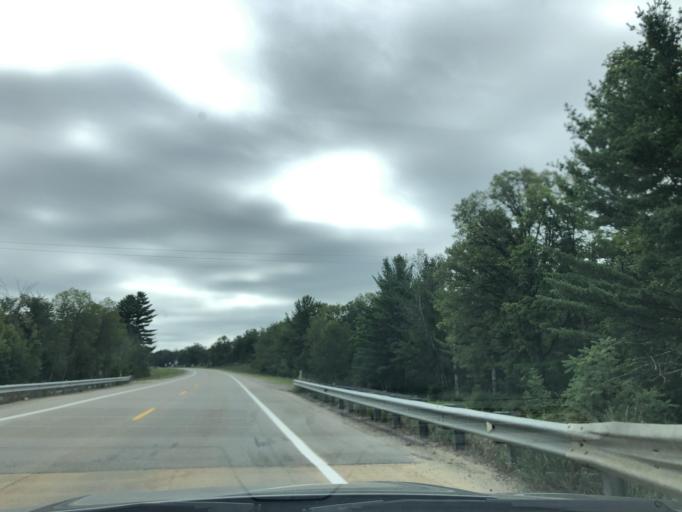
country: US
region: Michigan
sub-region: Clare County
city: Harrison
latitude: 44.0372
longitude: -85.0335
